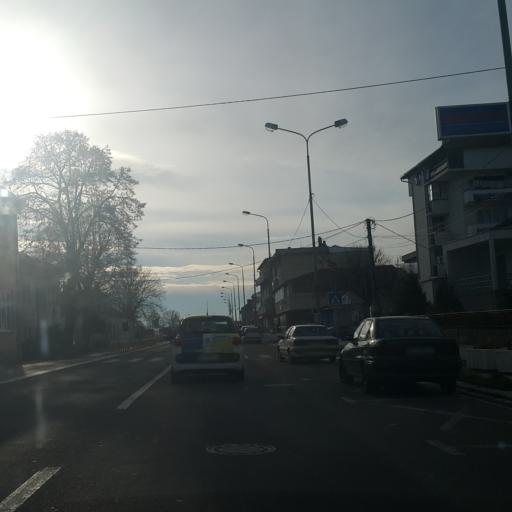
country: RS
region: Central Serbia
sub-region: Kolubarski Okrug
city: Lajkovac
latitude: 44.3685
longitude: 20.1647
